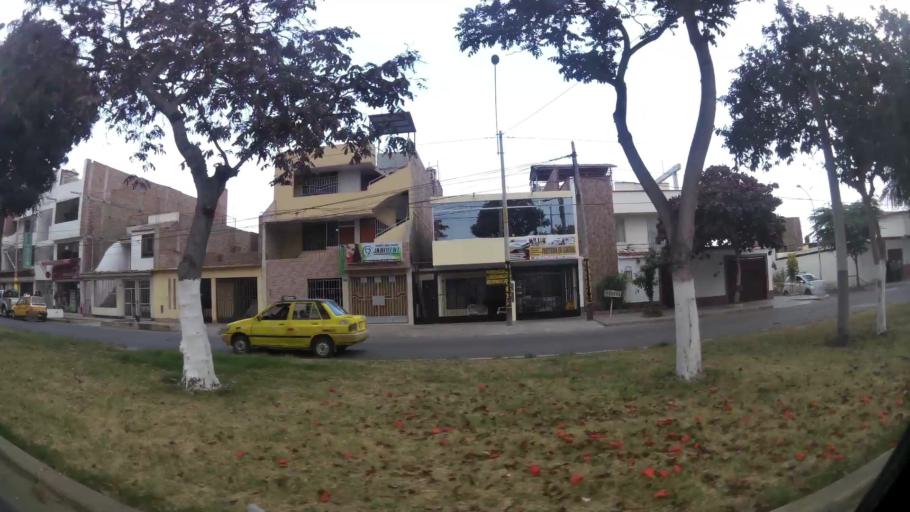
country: PE
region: La Libertad
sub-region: Provincia de Trujillo
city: La Esperanza
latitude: -8.0942
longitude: -79.0379
